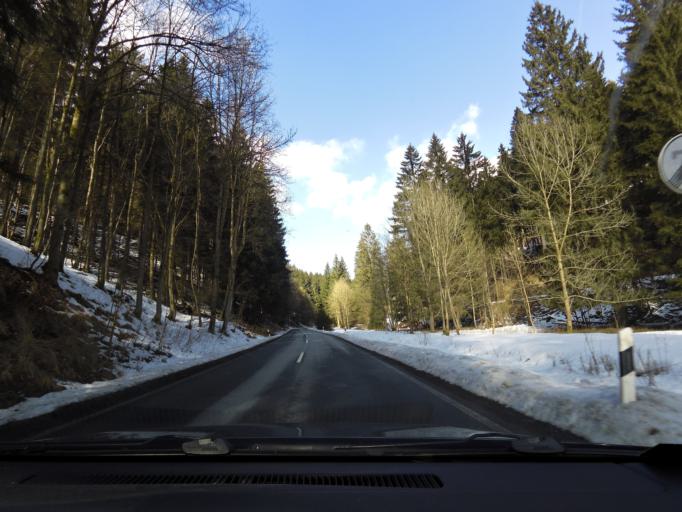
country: DE
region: Lower Saxony
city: Sankt Andreasberg
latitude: 51.6787
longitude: 10.4996
